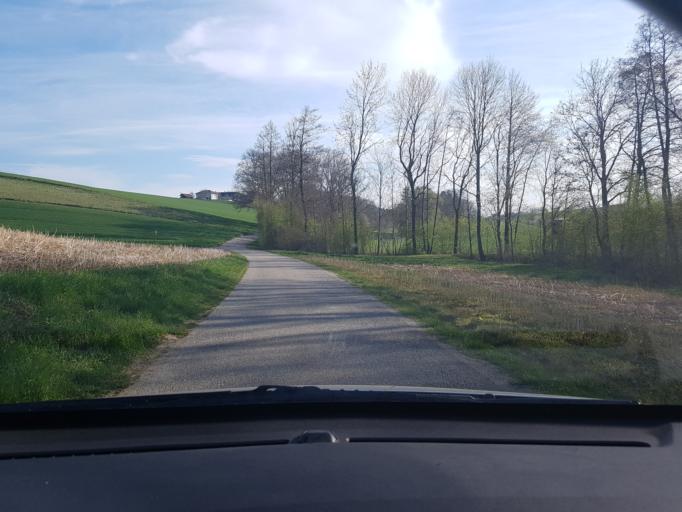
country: AT
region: Upper Austria
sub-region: Politischer Bezirk Linz-Land
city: Ansfelden
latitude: 48.1807
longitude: 14.3296
